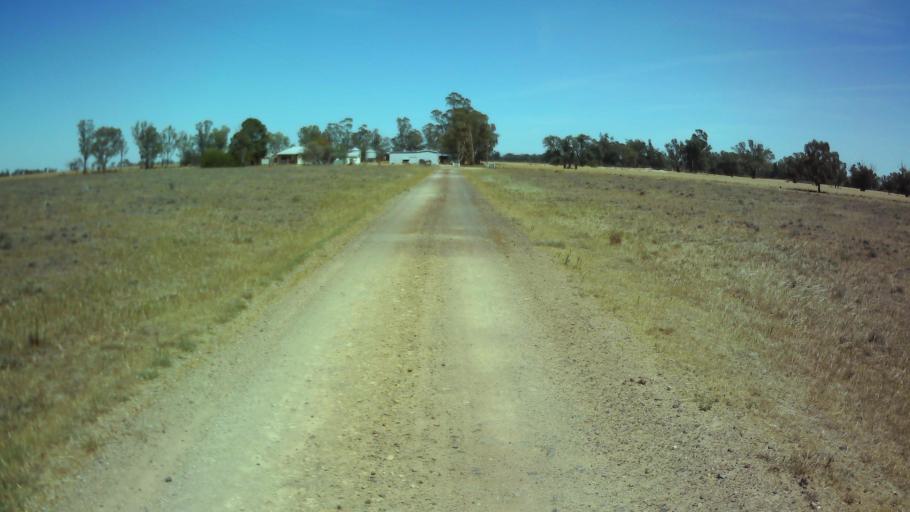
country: AU
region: New South Wales
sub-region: Weddin
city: Grenfell
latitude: -34.0481
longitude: 147.9192
